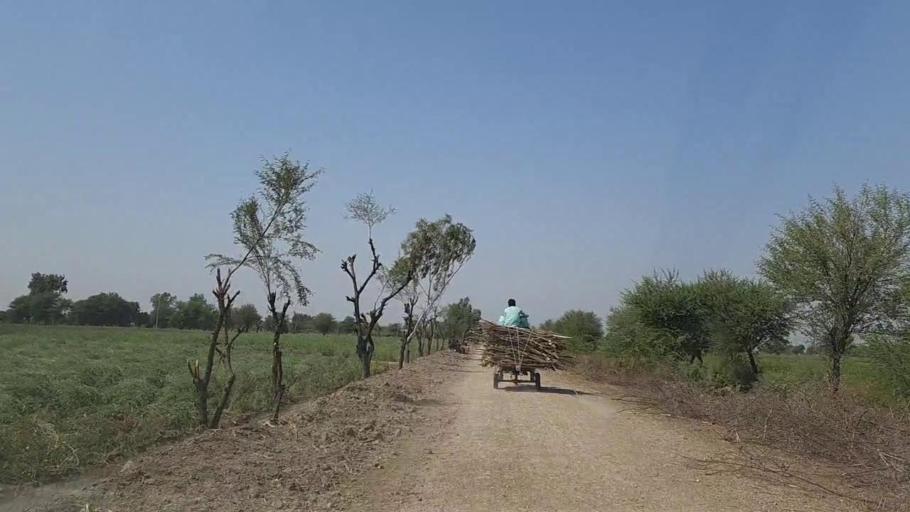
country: PK
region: Sindh
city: Samaro
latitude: 25.2264
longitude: 69.3952
